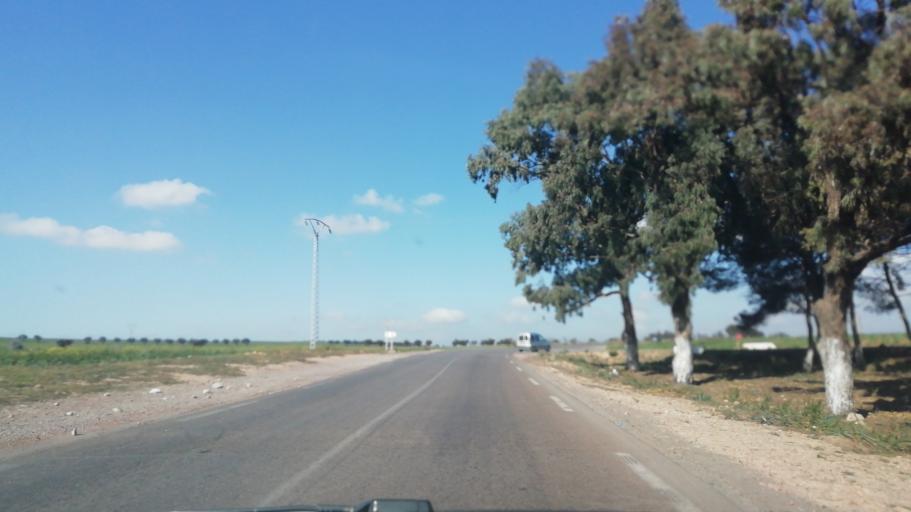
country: DZ
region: Oran
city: Ain el Bya
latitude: 35.7144
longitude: -0.2308
